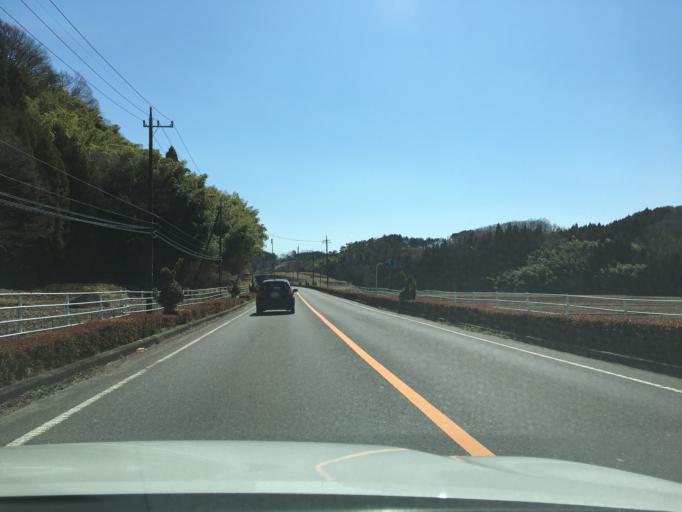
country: JP
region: Tochigi
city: Kuroiso
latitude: 37.0333
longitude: 140.1732
